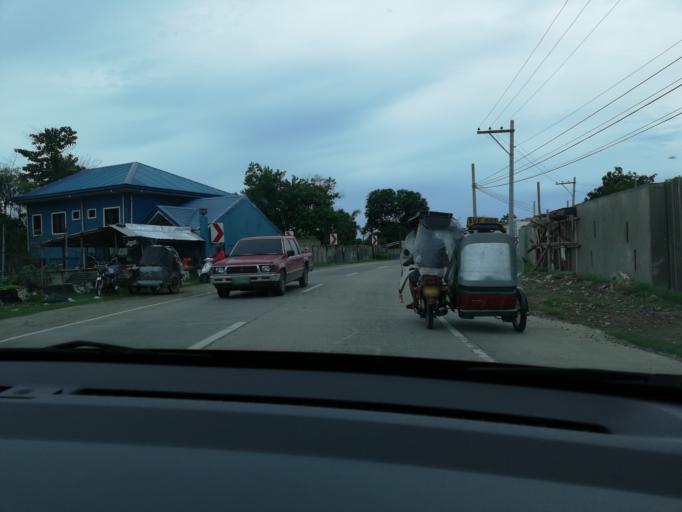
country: PH
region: Ilocos
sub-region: Province of Ilocos Sur
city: Vigan
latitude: 17.5820
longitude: 120.3771
